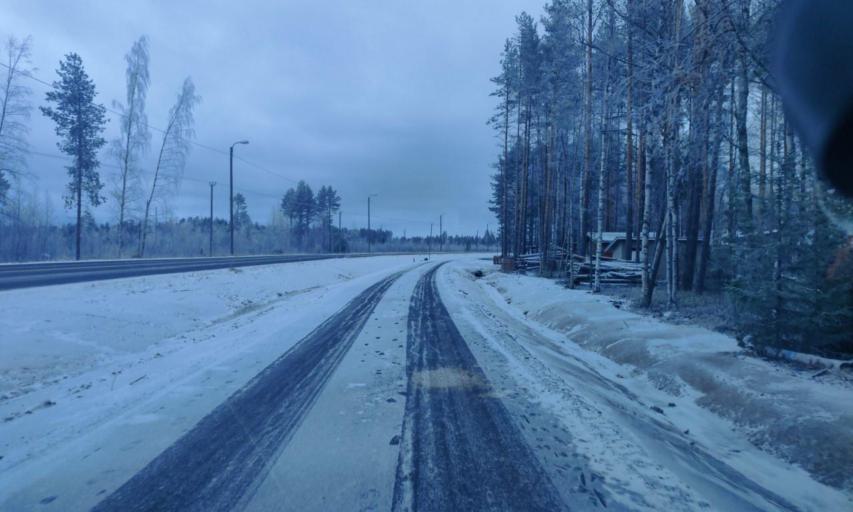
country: FI
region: Northern Ostrobothnia
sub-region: Oulu
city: Oulunsalo
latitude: 64.9881
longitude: 25.2591
